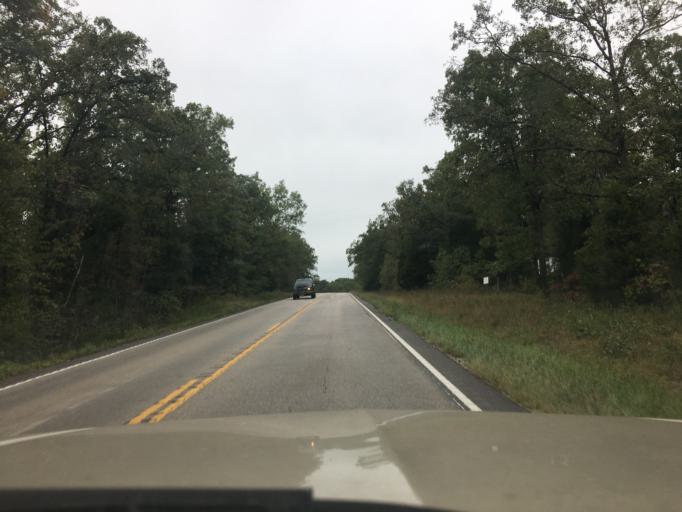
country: US
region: Missouri
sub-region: Gasconade County
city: Owensville
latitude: 38.2070
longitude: -91.4458
